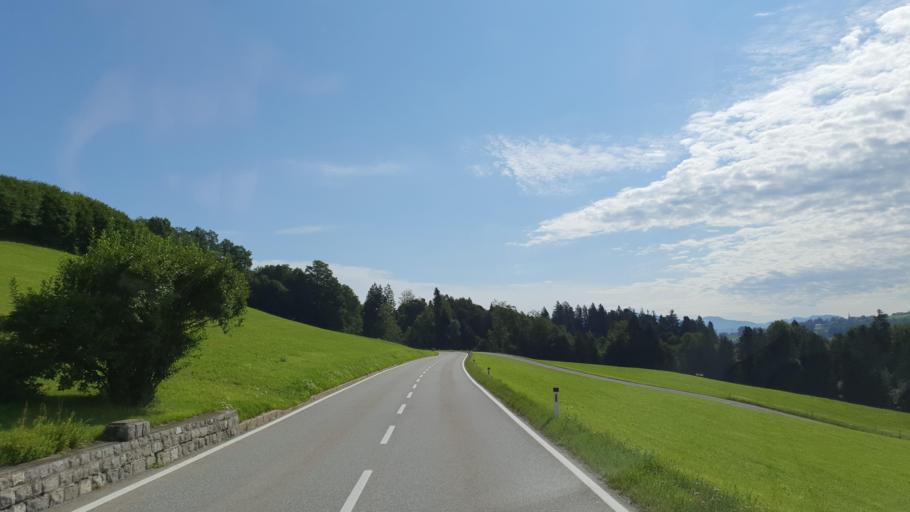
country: AT
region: Vorarlberg
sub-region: Politischer Bezirk Bregenz
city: Kennelbach
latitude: 47.4903
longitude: 9.7804
